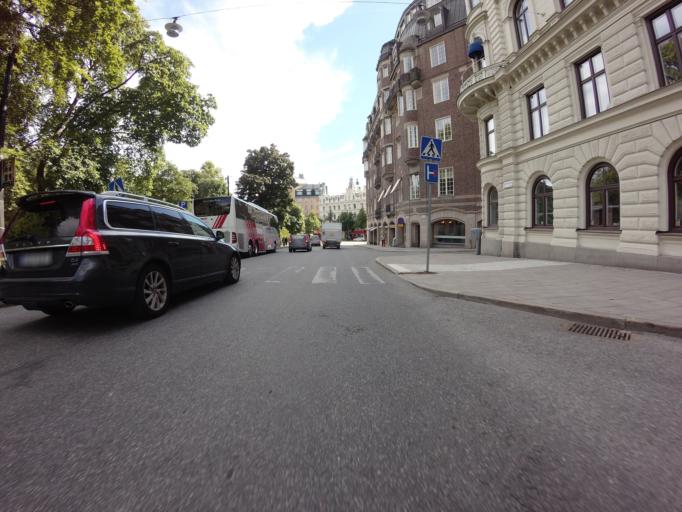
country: SE
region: Stockholm
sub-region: Stockholms Kommun
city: Stockholm
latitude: 59.3387
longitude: 18.0700
